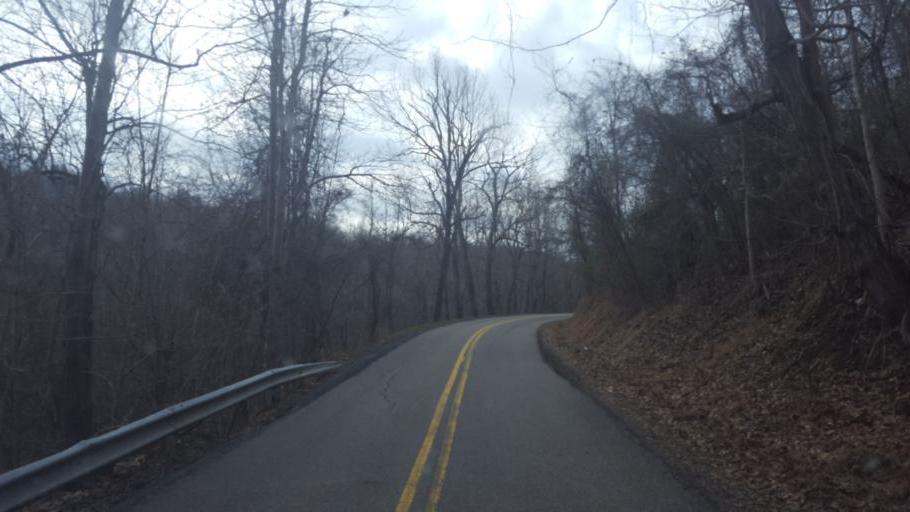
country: US
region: Ohio
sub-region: Gallia County
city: Gallipolis
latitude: 38.7165
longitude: -82.3333
